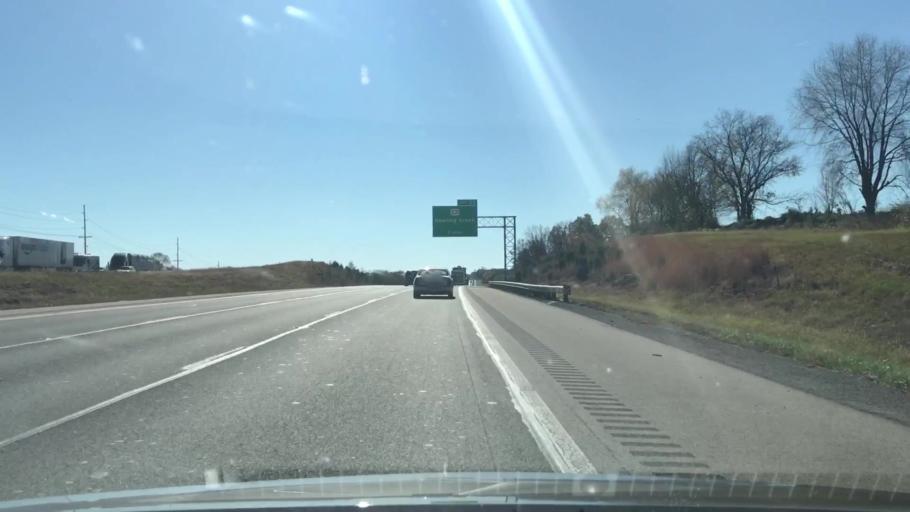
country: US
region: Kentucky
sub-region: Warren County
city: Bowling Green
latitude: 36.9648
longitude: -86.3986
